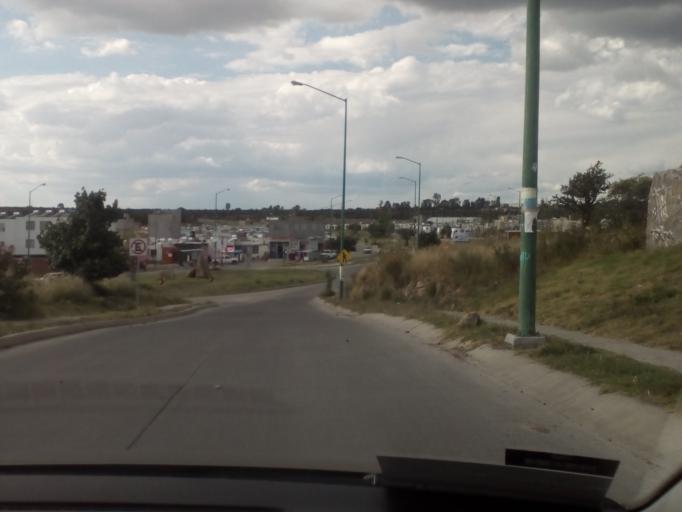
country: MX
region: Guanajuato
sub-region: Leon
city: Fraccionamiento Paseo de las Torres
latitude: 21.1878
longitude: -101.7644
